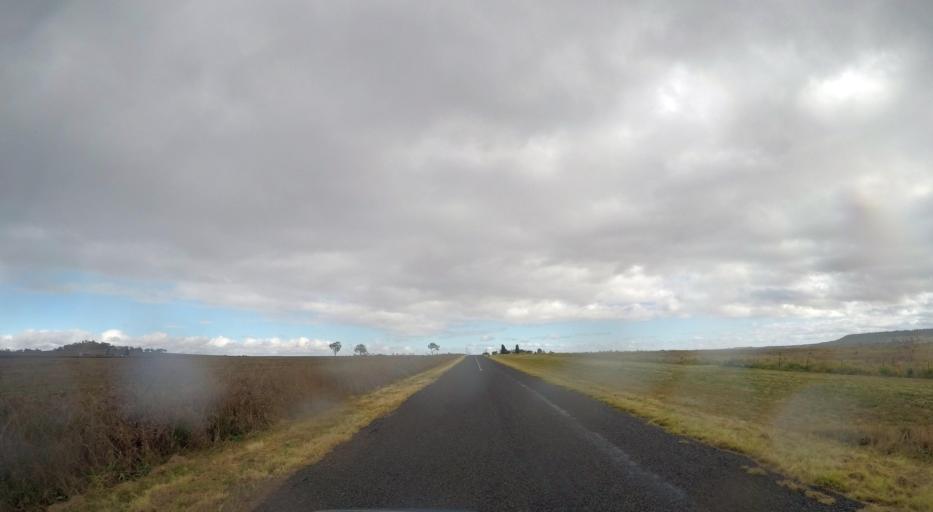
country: AU
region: Queensland
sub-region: Southern Downs
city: Warwick
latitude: -28.0497
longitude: 152.0377
